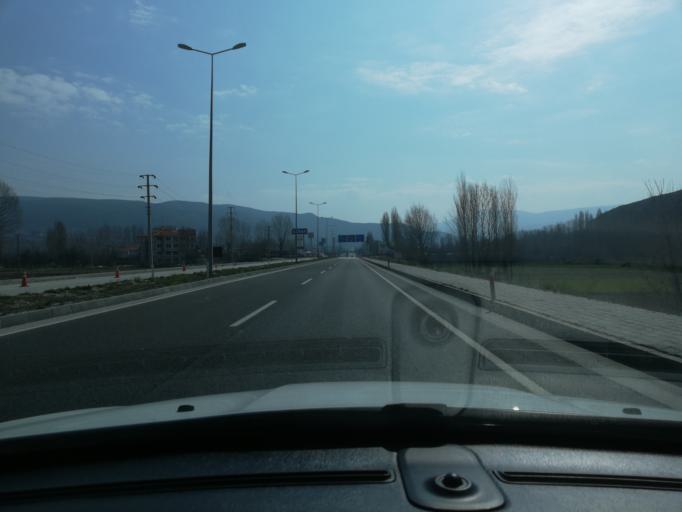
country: TR
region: Cankiri
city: Ilgaz
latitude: 40.9068
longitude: 33.6425
